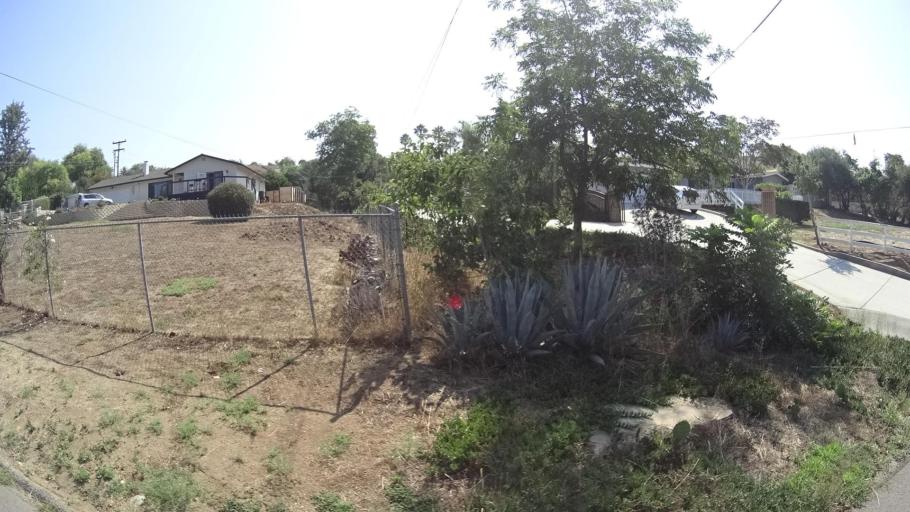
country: US
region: California
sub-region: San Diego County
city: Vista
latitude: 33.2439
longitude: -117.2432
